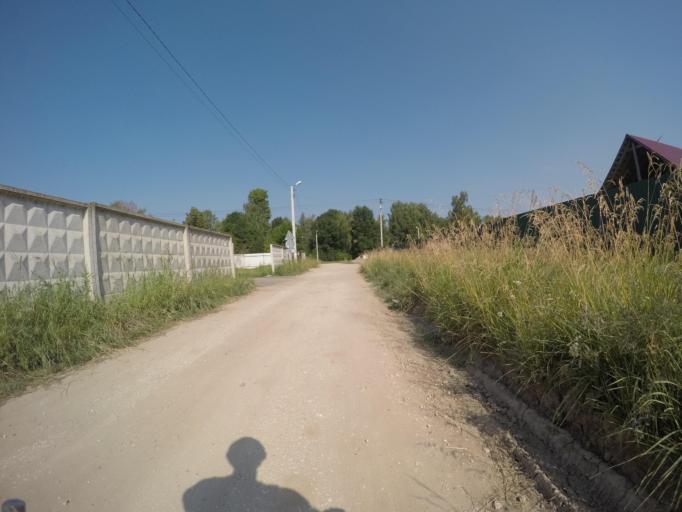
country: RU
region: Moskovskaya
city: Rechitsy
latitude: 55.6129
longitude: 38.5195
